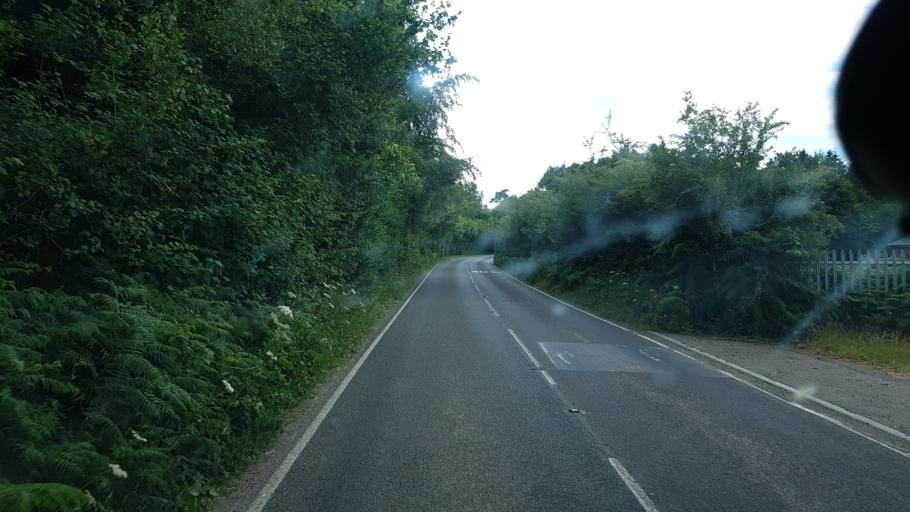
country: GB
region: England
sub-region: West Sussex
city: Furnace Green
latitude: 51.0641
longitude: -0.1697
